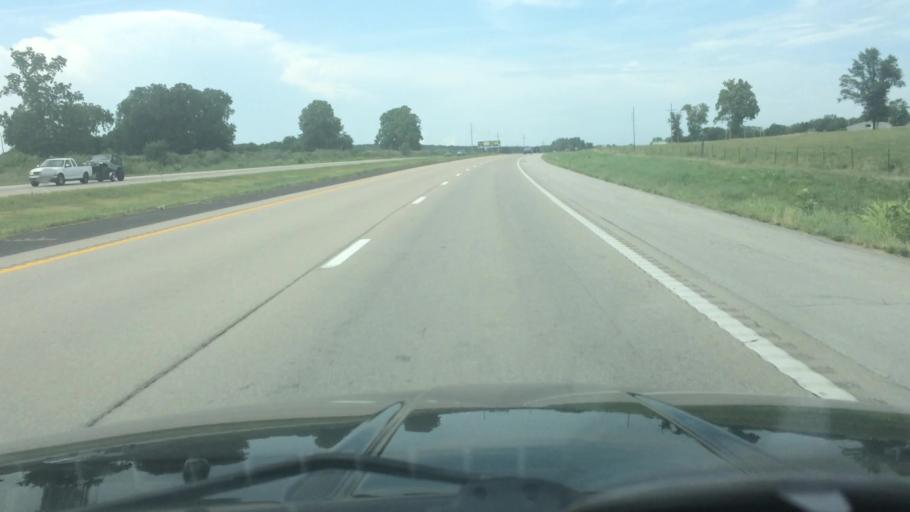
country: US
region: Missouri
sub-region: Polk County
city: Humansville
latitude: 37.8244
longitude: -93.6166
